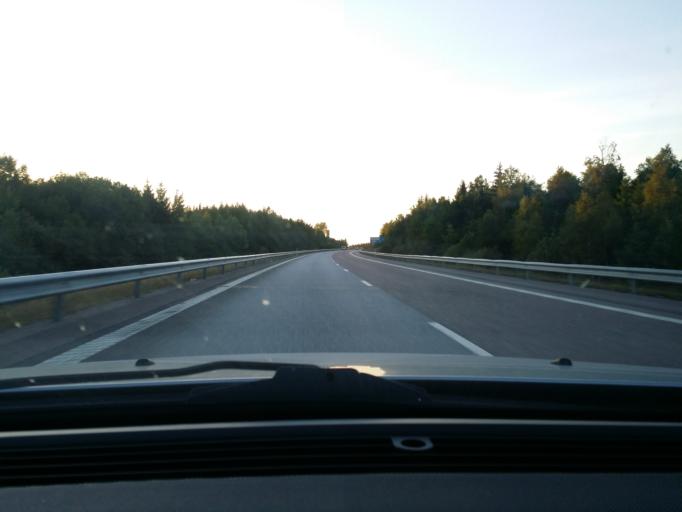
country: SE
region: Uppsala
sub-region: Enkopings Kommun
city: Dalby
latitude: 59.6151
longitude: 17.4064
